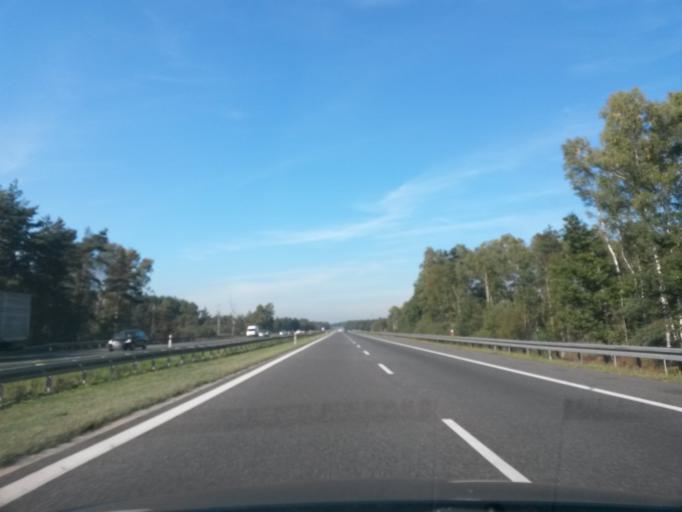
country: PL
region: Lesser Poland Voivodeship
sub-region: Powiat chrzanowski
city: Bolecin
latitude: 50.1180
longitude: 19.4989
